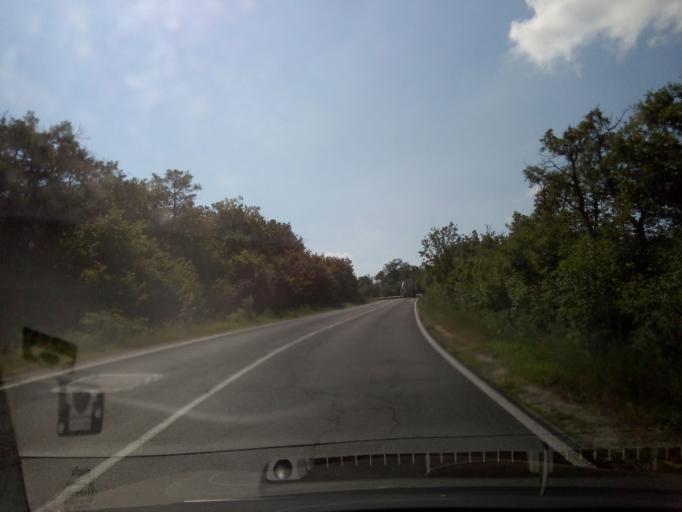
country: BG
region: Burgas
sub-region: Obshtina Nesebur
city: Sveti Vlas
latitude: 42.7477
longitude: 27.7514
